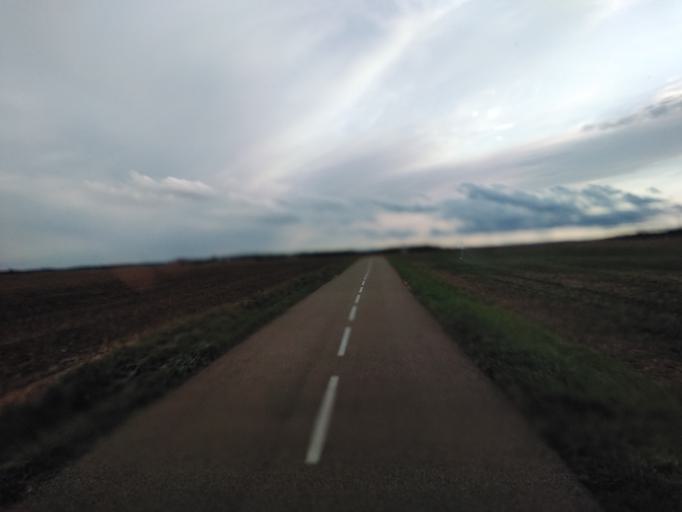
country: FR
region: Bourgogne
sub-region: Departement de l'Yonne
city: Ravieres
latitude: 47.7617
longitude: 4.3566
